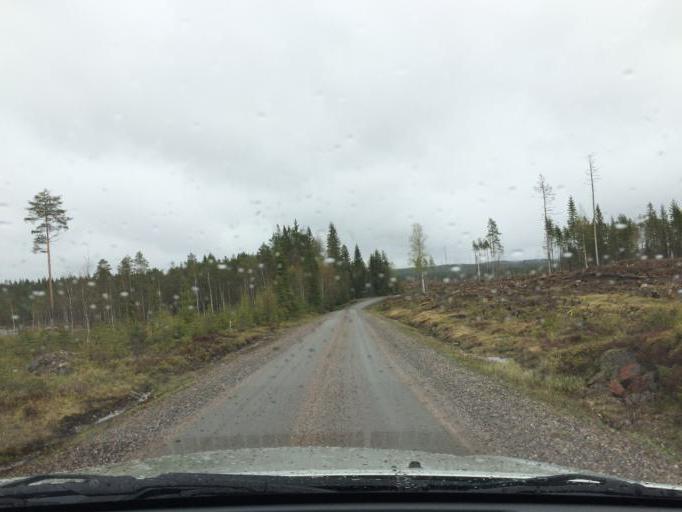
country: SE
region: Dalarna
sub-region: Ludvika Kommun
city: Abborrberget
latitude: 60.0176
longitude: 14.5962
